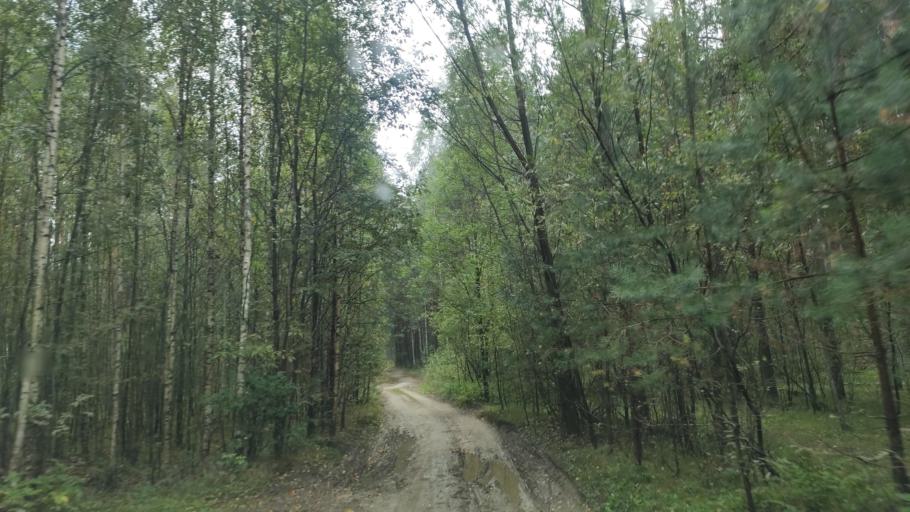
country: RU
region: Nizjnij Novgorod
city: Taremskoye
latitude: 56.0005
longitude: 42.9809
